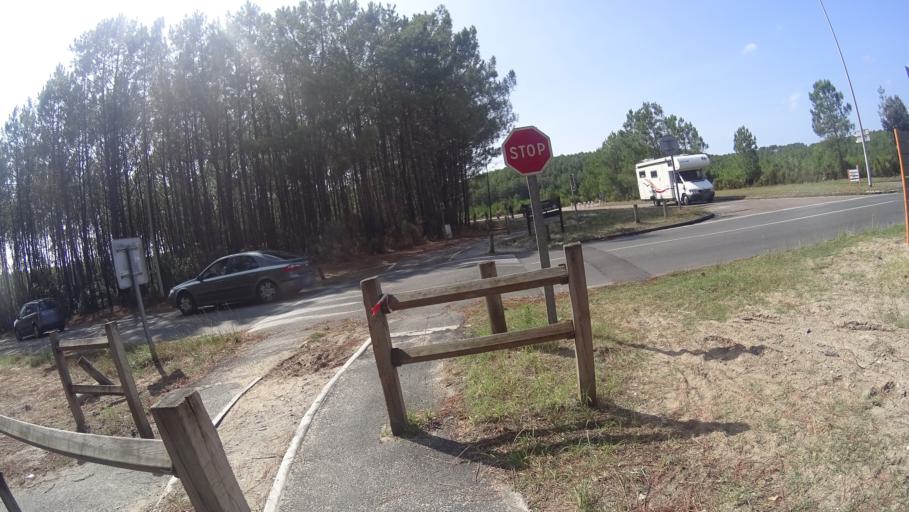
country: FR
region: Aquitaine
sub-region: Departement de la Gironde
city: Lacanau
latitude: 44.9856
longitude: -1.1440
